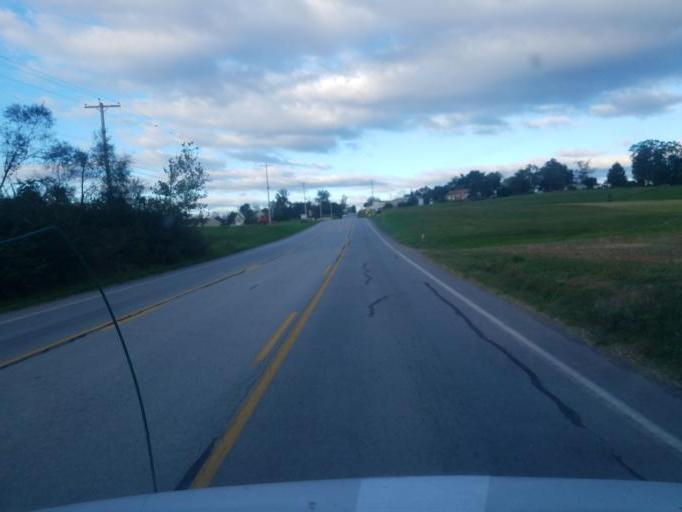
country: US
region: Pennsylvania
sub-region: Adams County
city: Lake Meade
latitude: 39.9363
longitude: -77.0415
